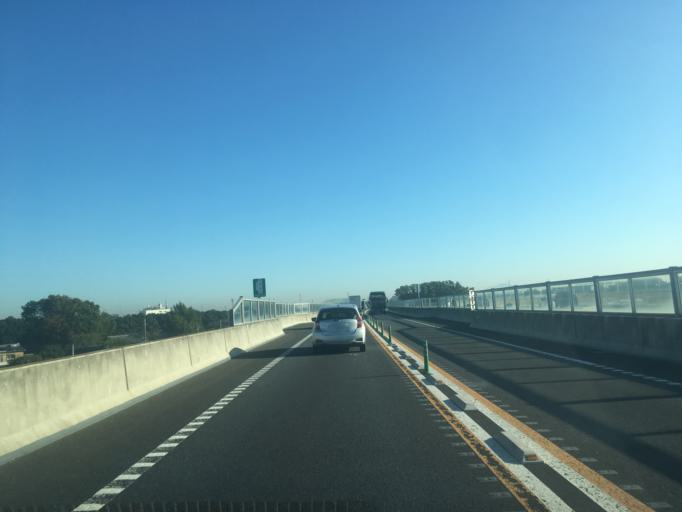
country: JP
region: Saitama
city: Kukichuo
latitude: 36.0542
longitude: 139.6903
